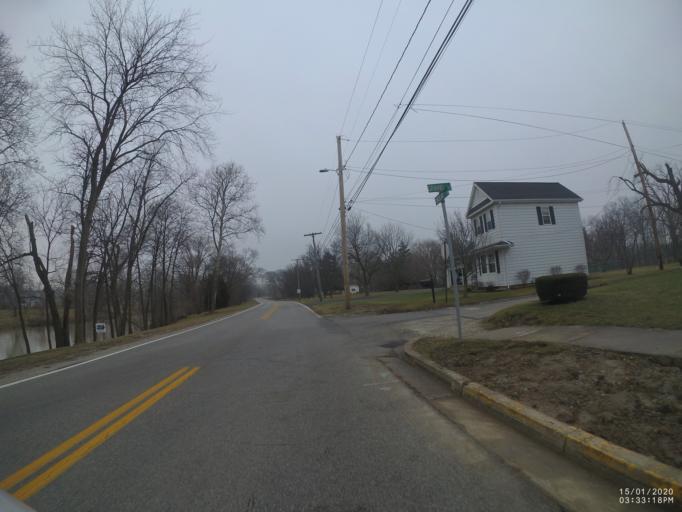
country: US
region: Ohio
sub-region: Sandusky County
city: Woodville
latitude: 41.4481
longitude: -83.3654
